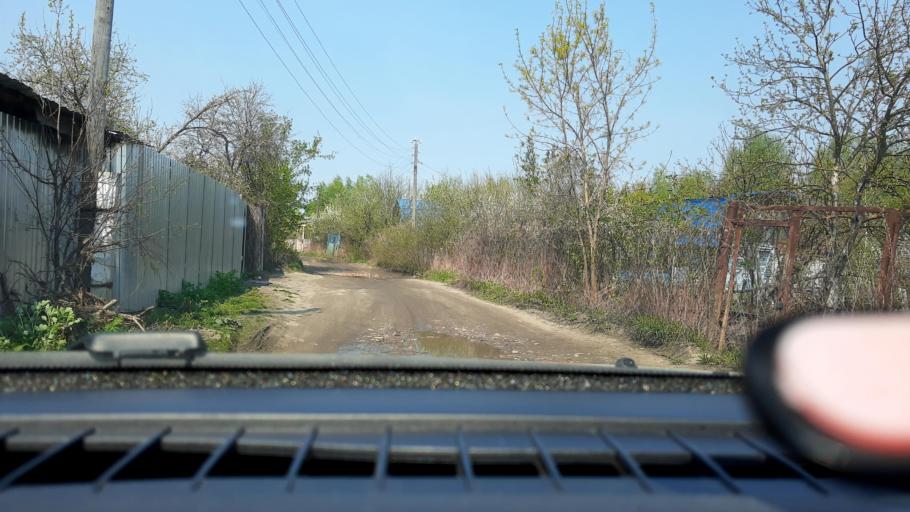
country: RU
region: Nizjnij Novgorod
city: Gorbatovka
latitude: 56.2673
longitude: 43.7852
